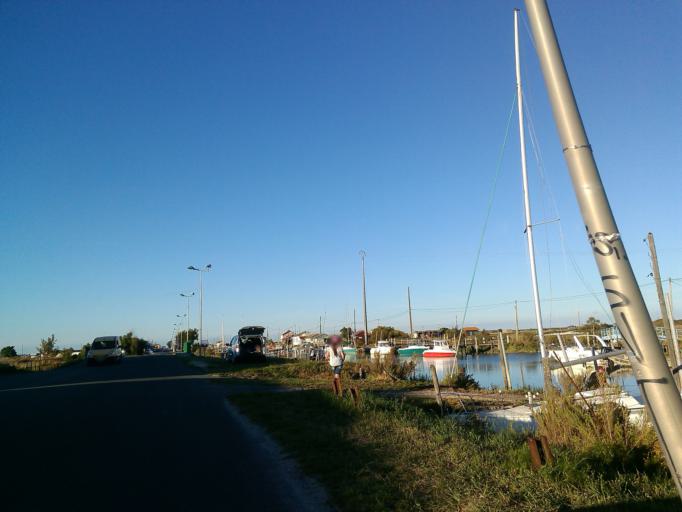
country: FR
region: Poitou-Charentes
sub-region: Departement de la Charente-Maritime
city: La Tremblade
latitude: 45.7714
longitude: -1.1322
